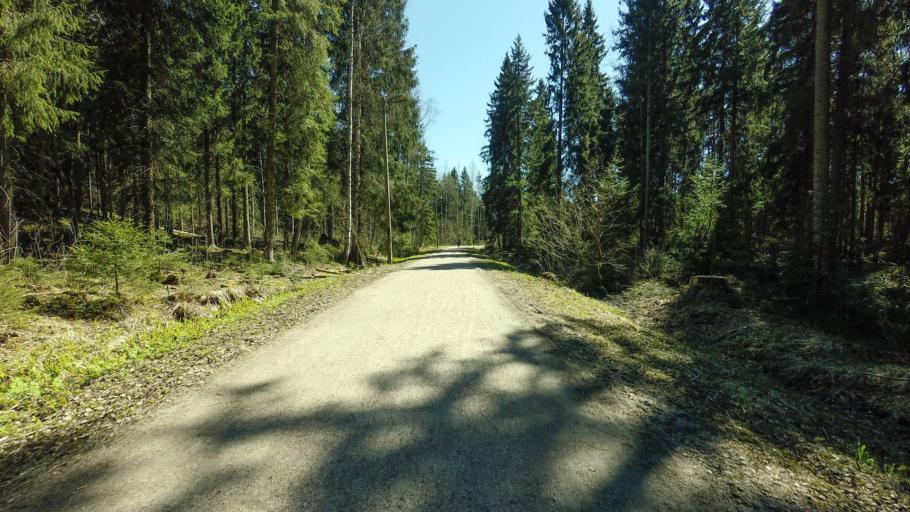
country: FI
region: Uusimaa
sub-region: Helsinki
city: Vantaa
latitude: 60.2272
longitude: 25.1467
